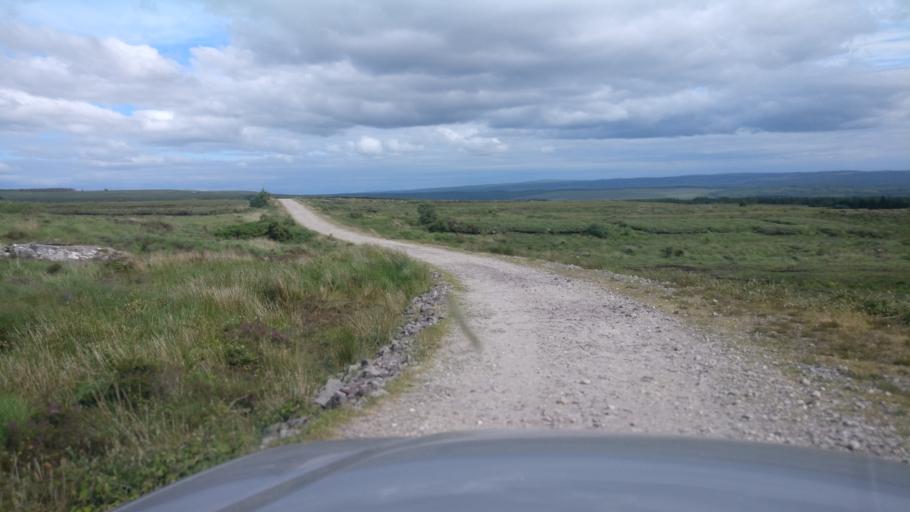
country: IE
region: Connaught
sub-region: County Galway
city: Gort
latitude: 53.0771
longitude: -8.6805
